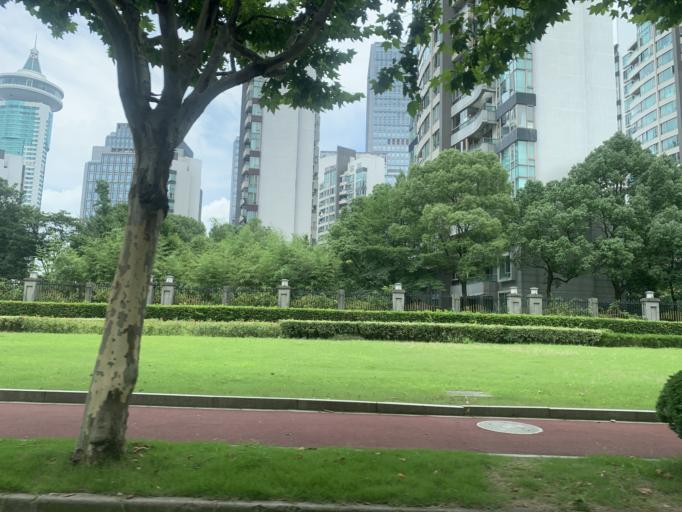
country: CN
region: Shanghai Shi
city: Huamu
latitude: 31.2145
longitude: 121.5343
